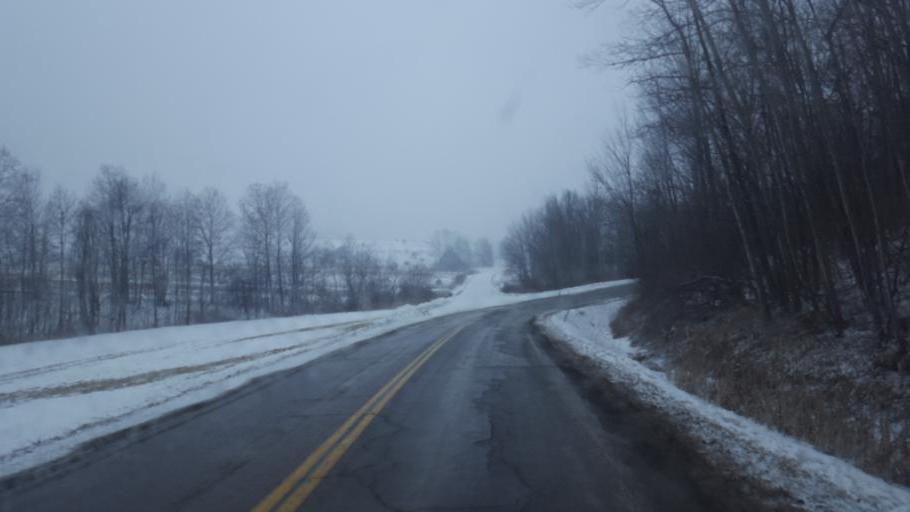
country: US
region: New York
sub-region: Steuben County
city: Canisteo
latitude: 42.1381
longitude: -77.5482
